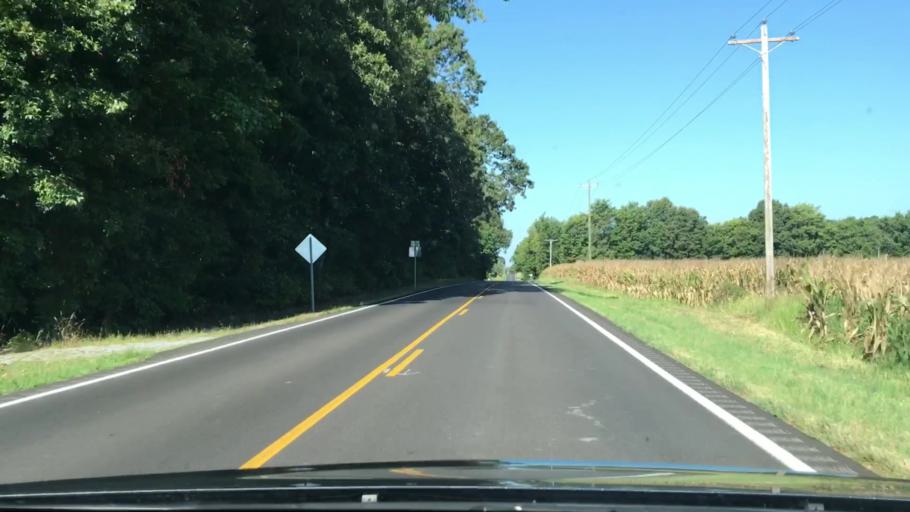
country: US
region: Kentucky
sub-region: Marshall County
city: Benton
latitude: 36.7649
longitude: -88.3714
